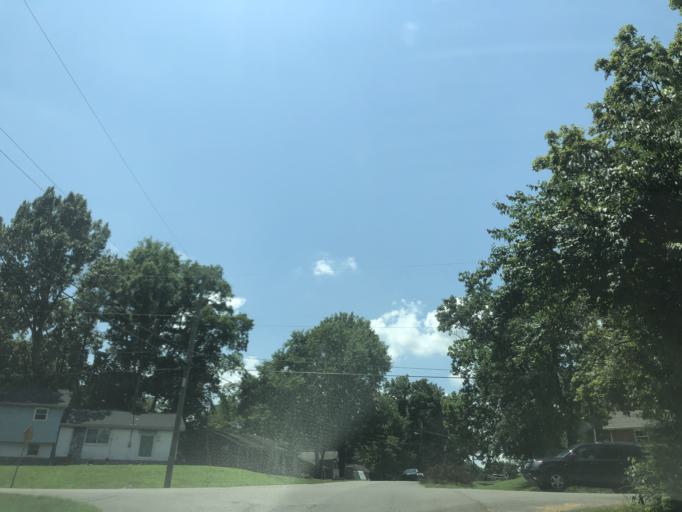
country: US
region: Tennessee
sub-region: Davidson County
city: Lakewood
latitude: 36.1901
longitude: -86.6175
